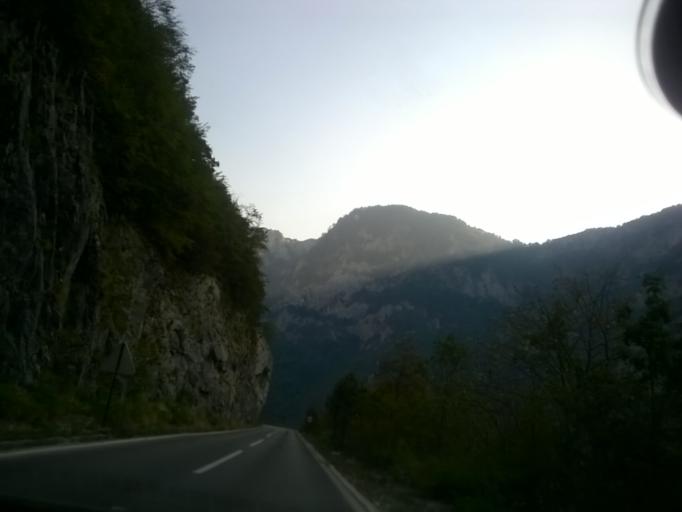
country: ME
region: Opstina Pluzine
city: Pluzine
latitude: 43.2263
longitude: 18.8461
